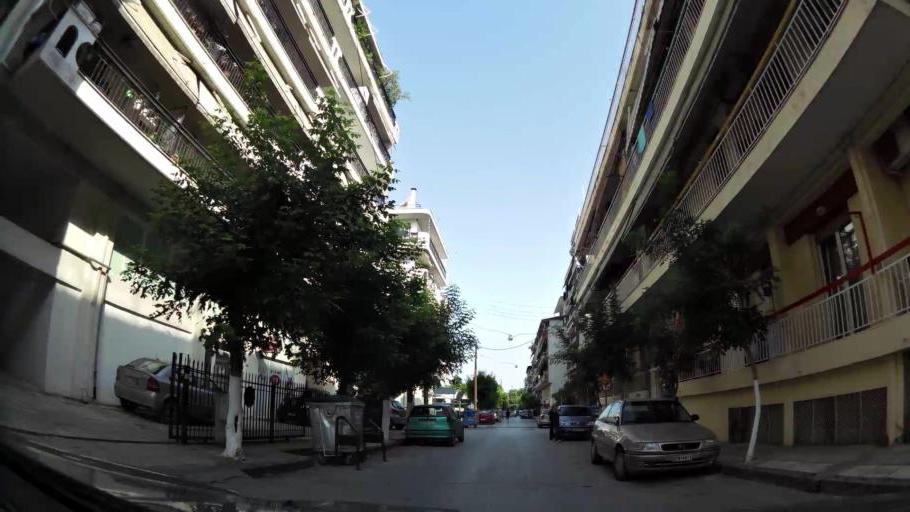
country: GR
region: Central Macedonia
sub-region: Nomos Thessalonikis
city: Menemeni
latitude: 40.6565
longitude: 22.9114
